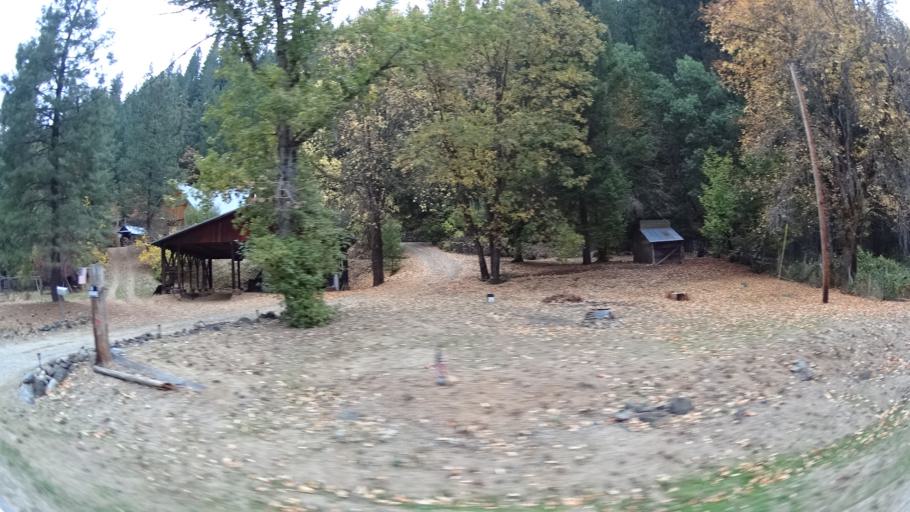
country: US
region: California
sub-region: Siskiyou County
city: Happy Camp
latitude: 41.8671
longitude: -123.4032
